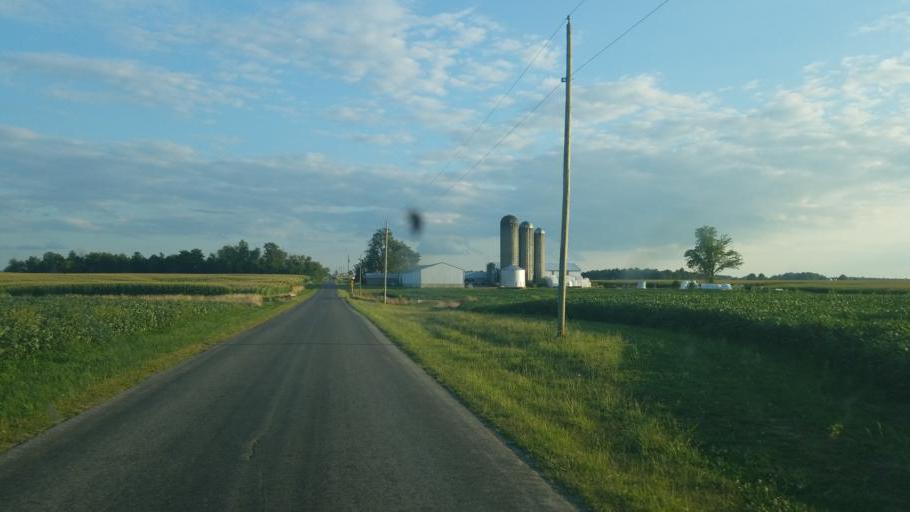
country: US
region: Ohio
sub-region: Huron County
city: Greenwich
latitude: 41.0081
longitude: -82.5592
